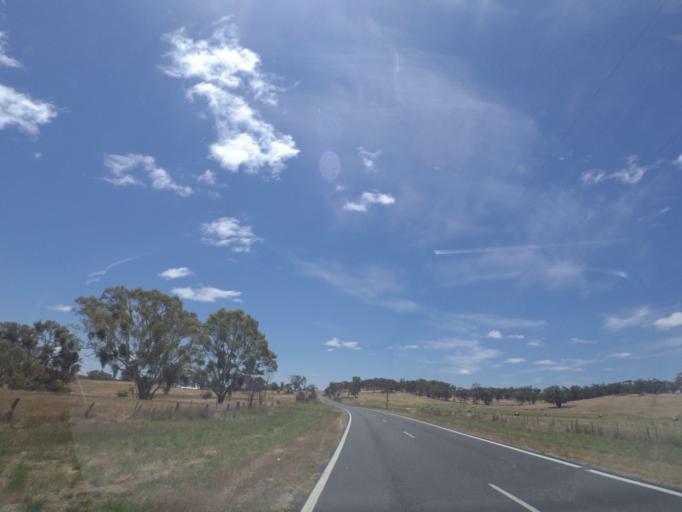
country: AU
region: Victoria
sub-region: Mount Alexander
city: Castlemaine
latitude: -37.2193
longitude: 144.1408
